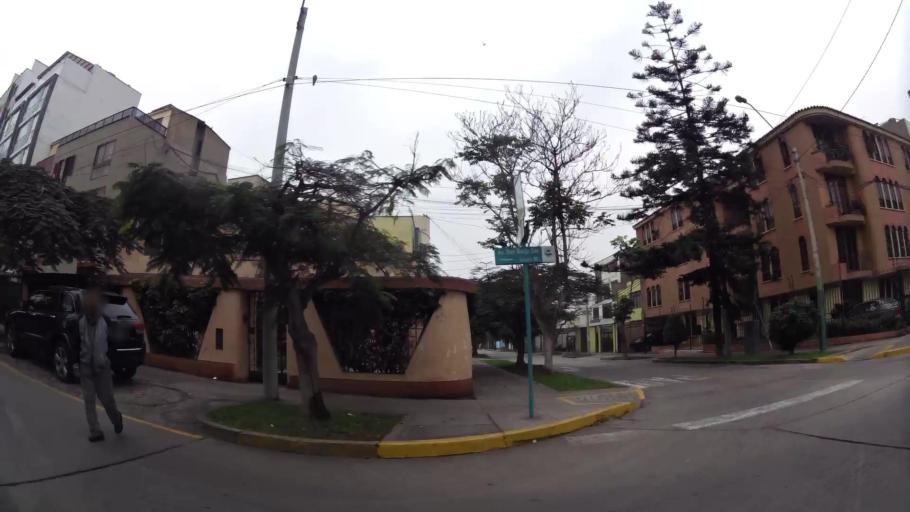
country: PE
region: Lima
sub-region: Lima
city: San Luis
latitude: -12.1010
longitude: -77.0008
